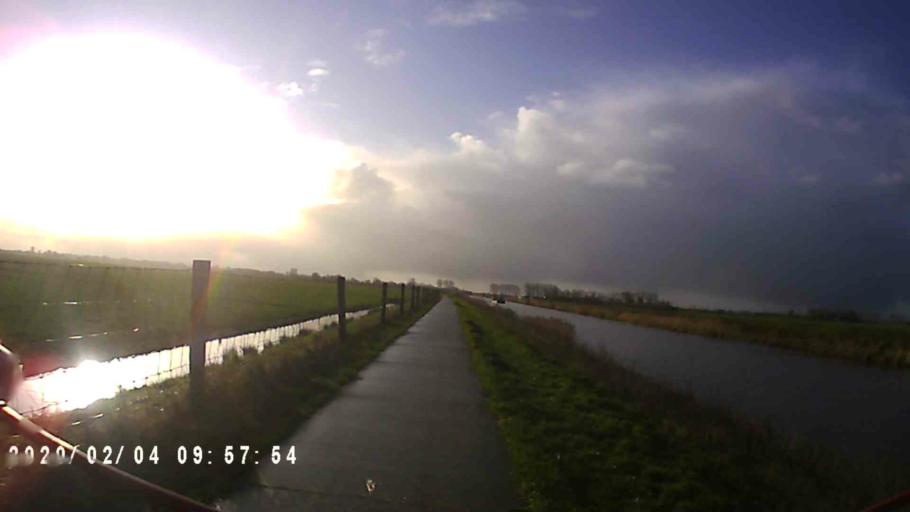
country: NL
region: Groningen
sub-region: Gemeente Zuidhorn
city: Aduard
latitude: 53.2666
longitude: 6.5098
